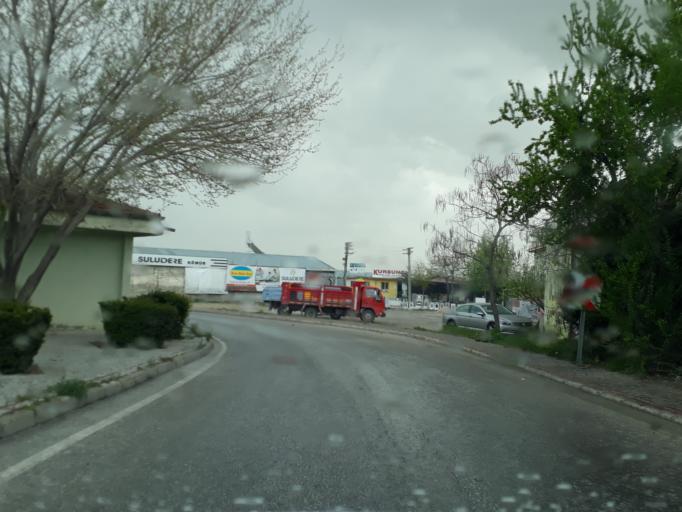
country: TR
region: Konya
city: Selcuklu
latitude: 37.9164
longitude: 32.4762
